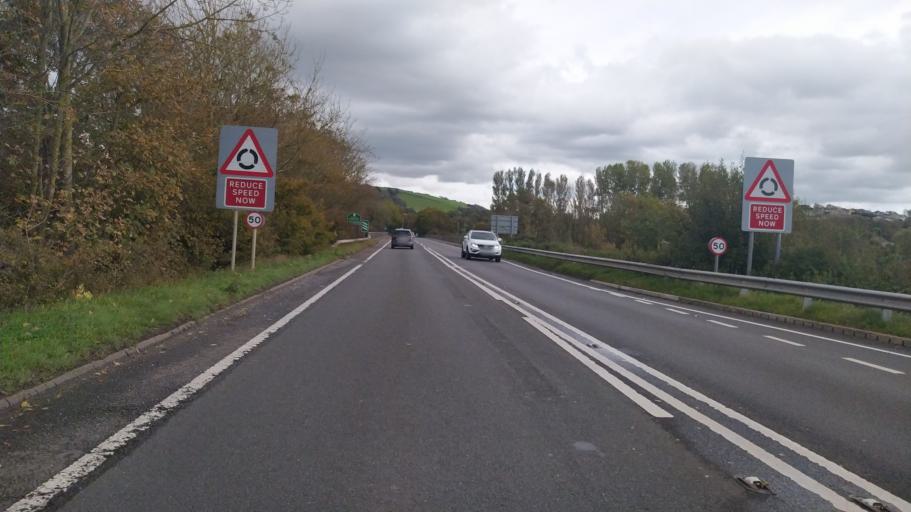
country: GB
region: England
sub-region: Dorset
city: Bridport
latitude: 50.7233
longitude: -2.7629
